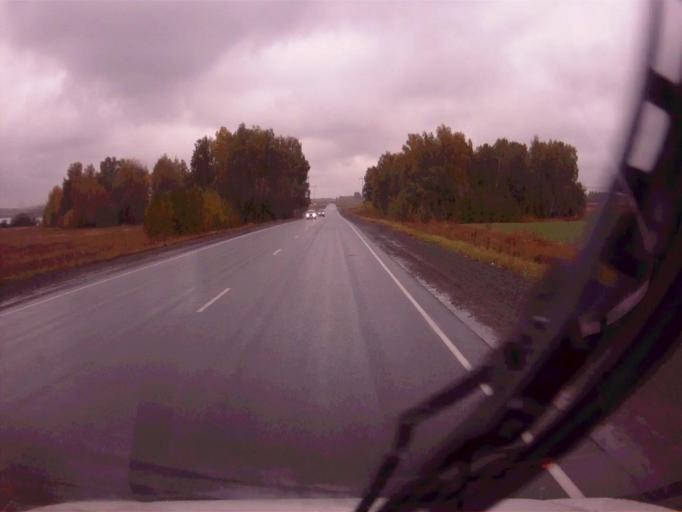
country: RU
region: Chelyabinsk
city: Roshchino
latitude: 55.3867
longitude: 61.1303
